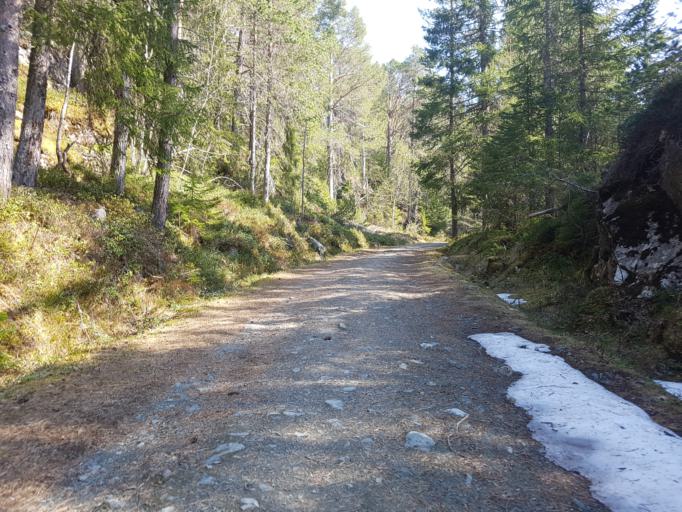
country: NO
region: Sor-Trondelag
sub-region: Trondheim
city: Trondheim
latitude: 63.4334
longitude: 10.2925
